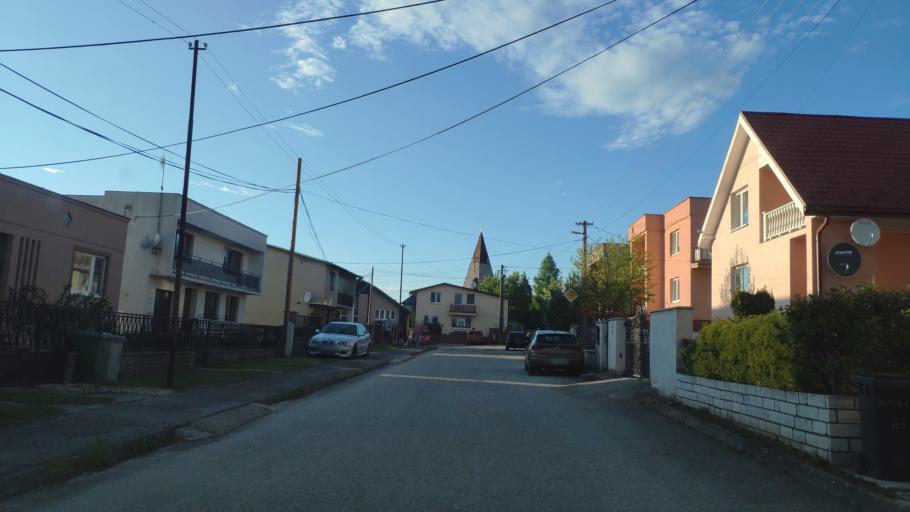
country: SK
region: Kosicky
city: Kosice
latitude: 48.7516
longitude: 21.3469
